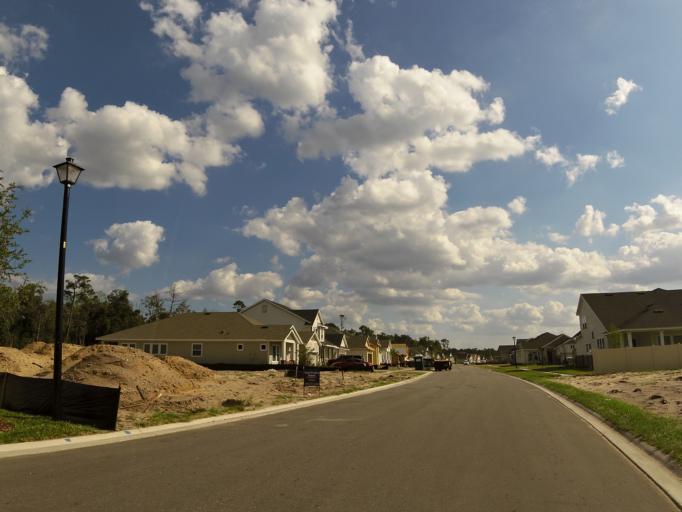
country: US
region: Florida
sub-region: Saint Johns County
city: Palm Valley
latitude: 30.1762
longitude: -81.5031
